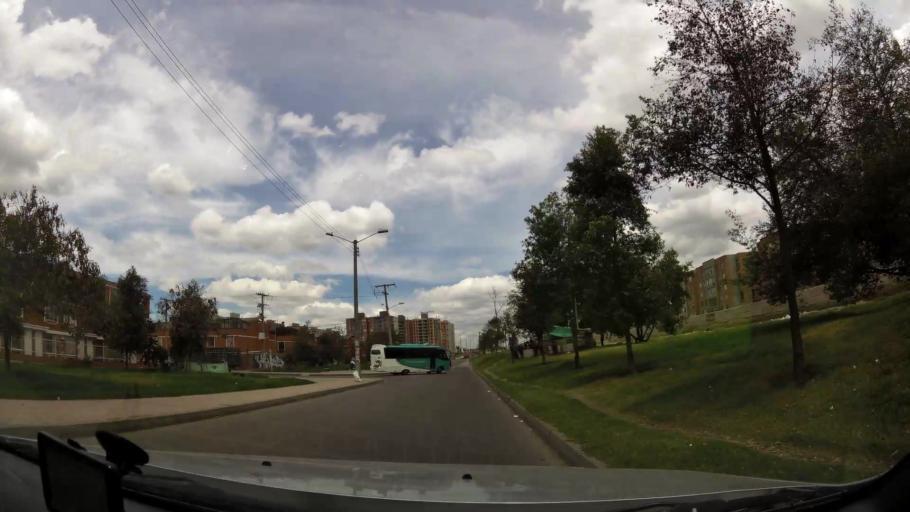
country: CO
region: Bogota D.C.
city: Bogota
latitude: 4.6519
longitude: -74.1504
